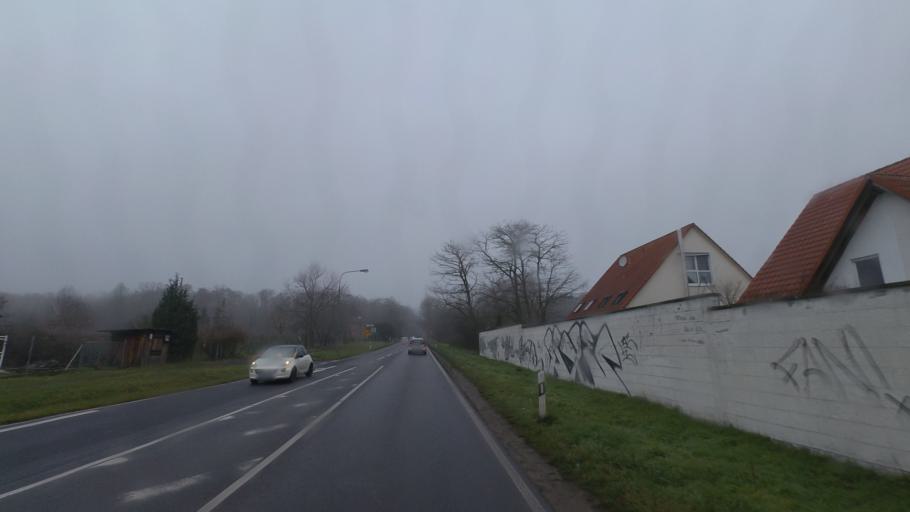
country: DE
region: Hesse
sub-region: Regierungsbezirk Darmstadt
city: Seligenstadt
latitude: 50.0553
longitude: 8.9262
